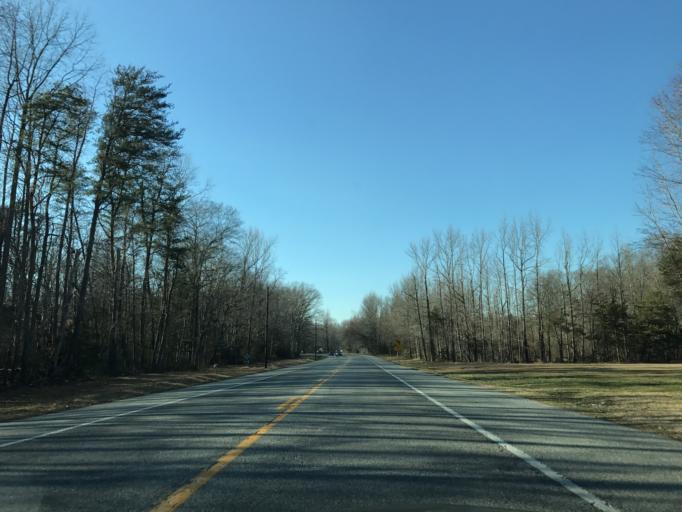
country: US
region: Maryland
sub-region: Caroline County
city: Greensboro
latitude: 39.0440
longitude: -75.8065
